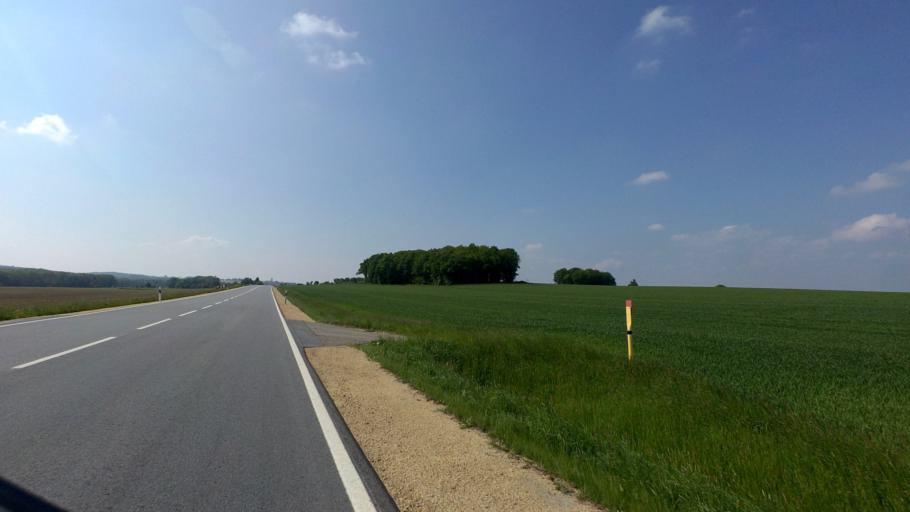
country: DE
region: Saxony
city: Hochkirch
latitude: 51.1308
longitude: 14.6140
